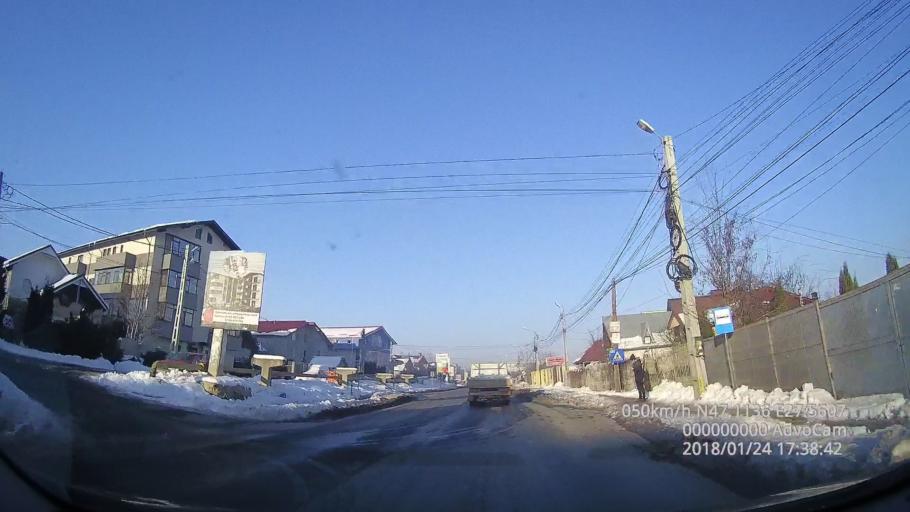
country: RO
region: Iasi
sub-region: Comuna Ciurea
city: Lunca Cetatuii
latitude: 47.1139
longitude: 27.5610
